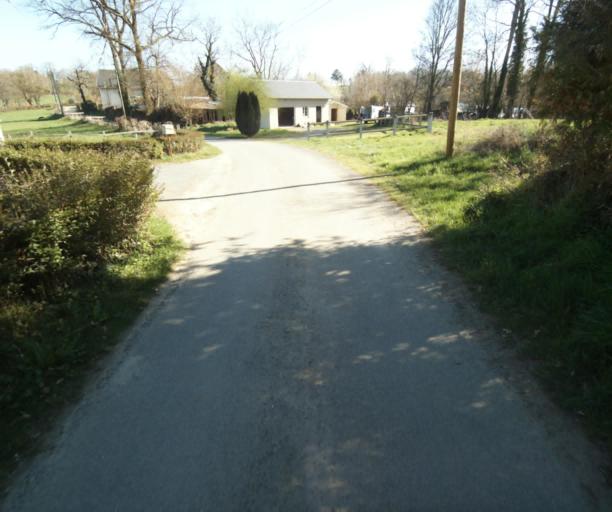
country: FR
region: Limousin
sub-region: Departement de la Correze
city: Chamboulive
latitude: 45.4327
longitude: 1.6488
